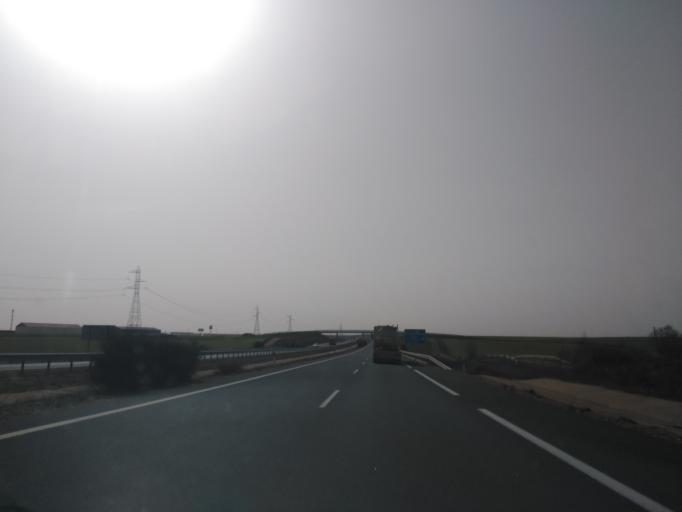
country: ES
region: Castille and Leon
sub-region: Provincia de Palencia
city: Marcilla de Campos
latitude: 42.3725
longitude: -4.3885
